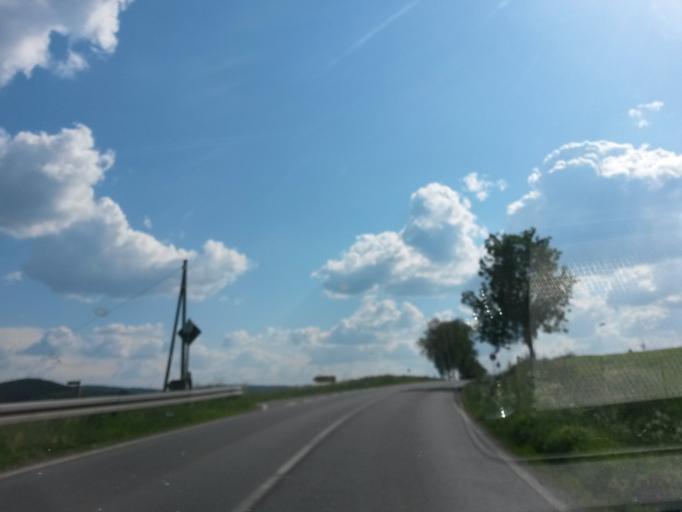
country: DE
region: North Rhine-Westphalia
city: Balve
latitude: 51.3003
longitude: 7.8537
